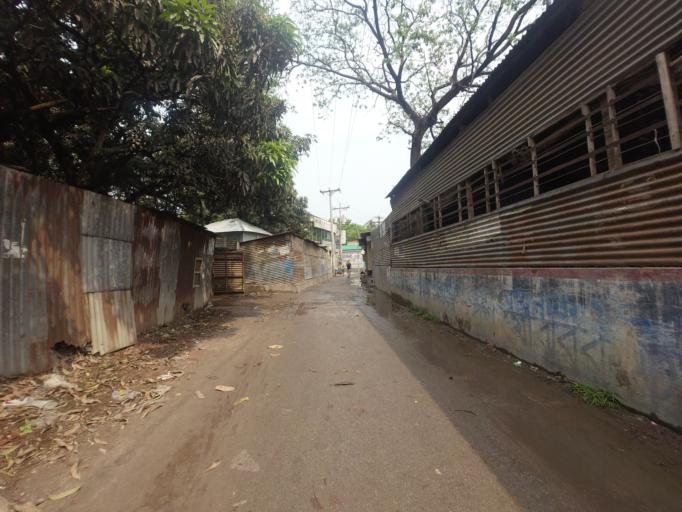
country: BD
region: Rajshahi
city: Sirajganj
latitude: 24.3270
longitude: 89.6891
